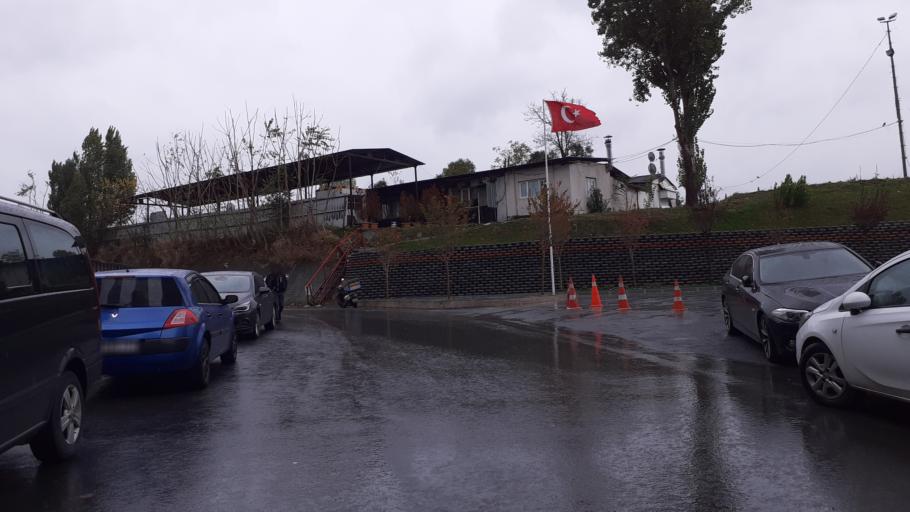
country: TR
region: Istanbul
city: Bahcelievler
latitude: 40.9899
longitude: 28.8355
